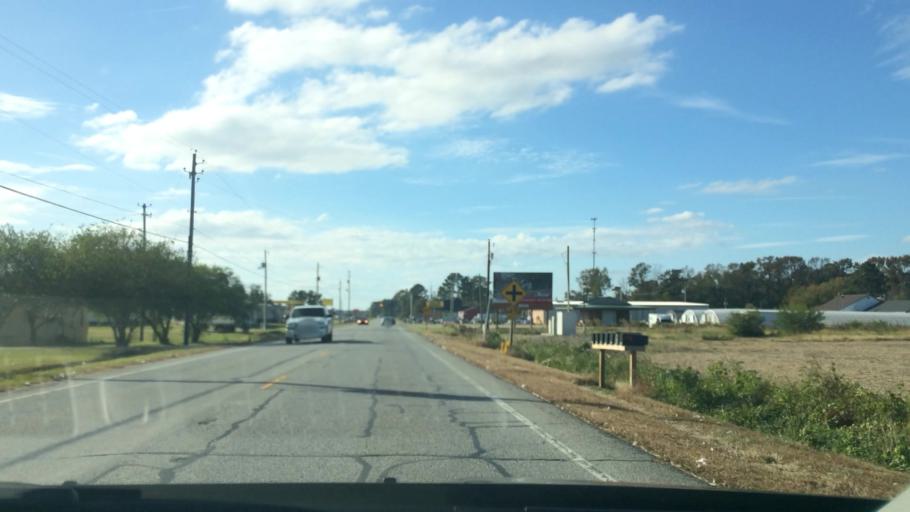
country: US
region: North Carolina
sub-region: Greene County
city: Snow Hill
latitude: 35.4400
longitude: -77.7889
